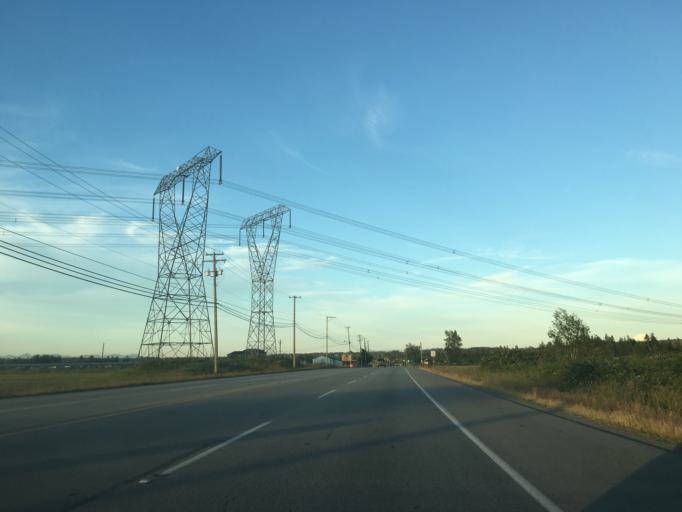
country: US
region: Washington
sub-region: Whatcom County
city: Blaine
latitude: 49.0165
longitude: -122.7439
